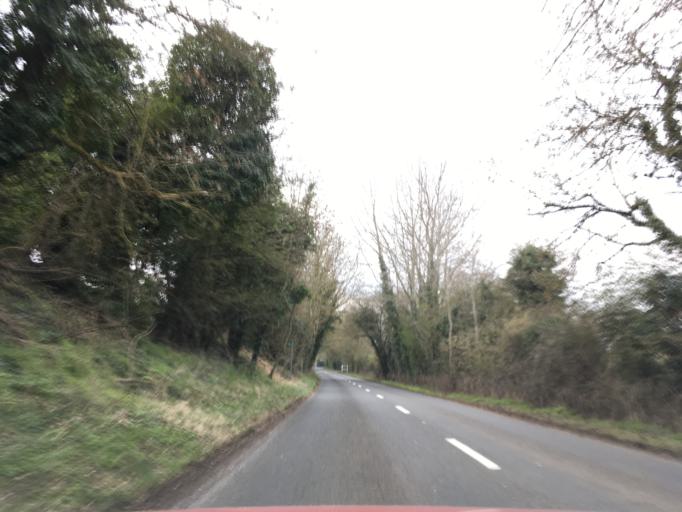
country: GB
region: England
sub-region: Gloucestershire
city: Bourton on the Water
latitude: 51.7882
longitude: -1.7669
